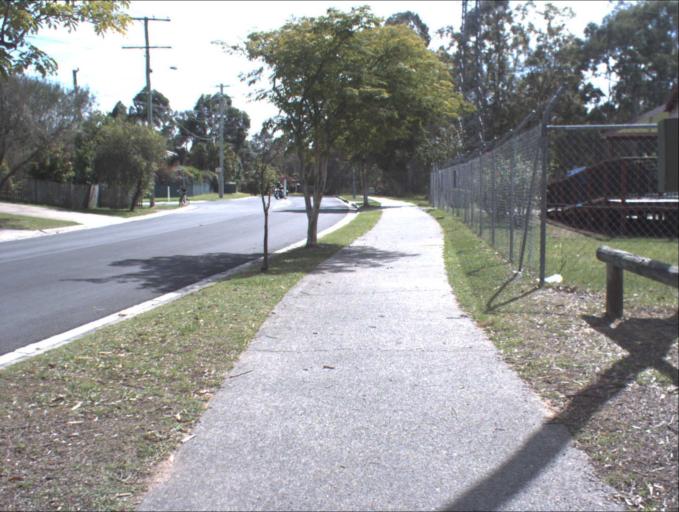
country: AU
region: Queensland
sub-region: Logan
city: Woodridge
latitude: -27.6690
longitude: 153.0595
